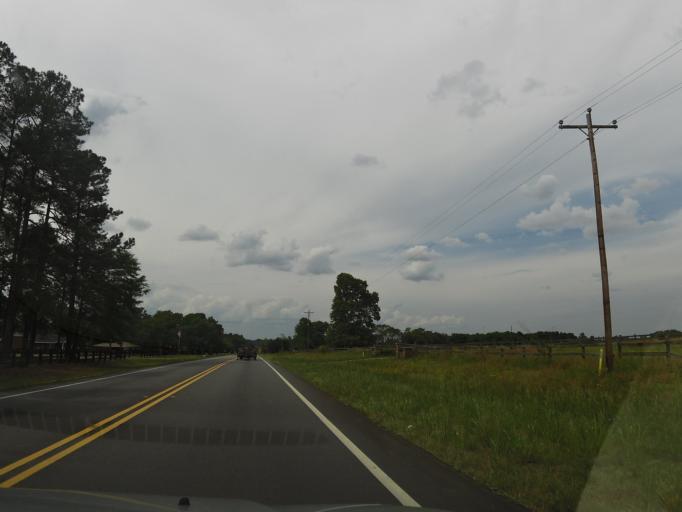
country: US
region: Georgia
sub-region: McDuffie County
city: Thomson
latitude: 33.4102
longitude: -82.4808
